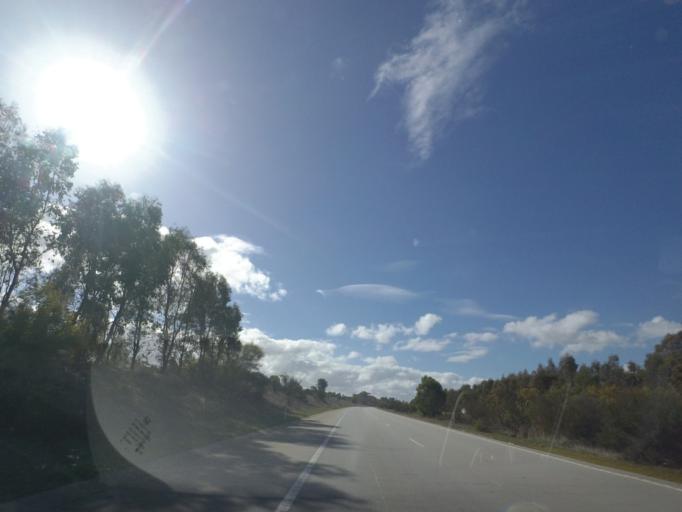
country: AU
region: New South Wales
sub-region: Albury Municipality
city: Lavington
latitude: -36.0305
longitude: 146.9768
